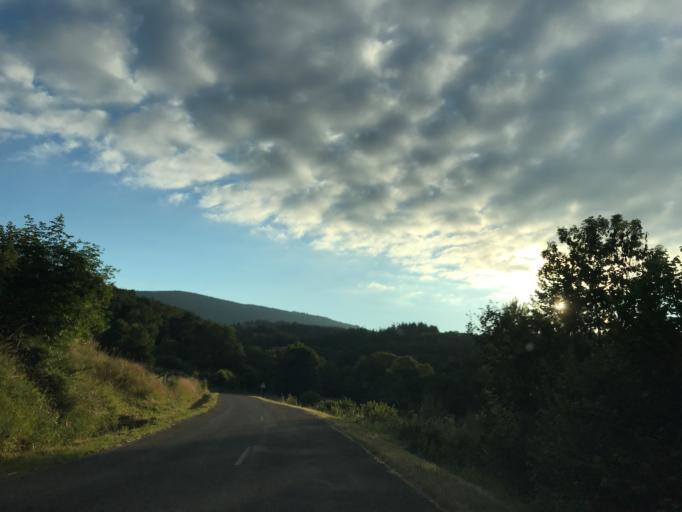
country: FR
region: Rhone-Alpes
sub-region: Departement de la Loire
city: Noiretable
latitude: 45.7739
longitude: 3.8134
